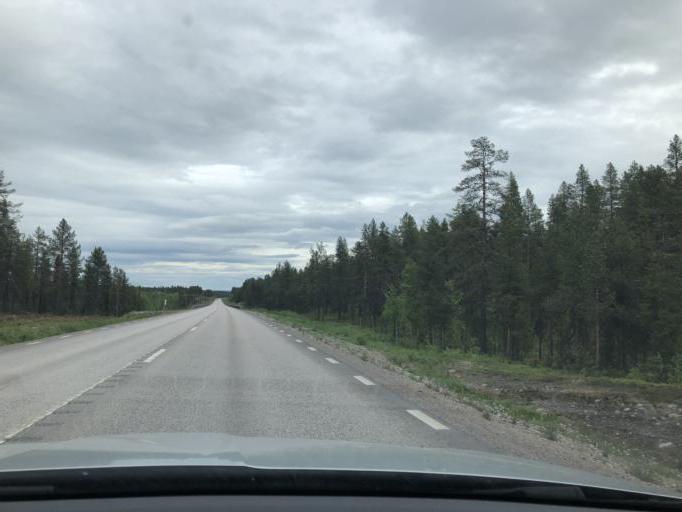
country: SE
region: Norrbotten
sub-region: Gallivare Kommun
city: Malmberget
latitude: 67.6392
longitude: 21.0877
